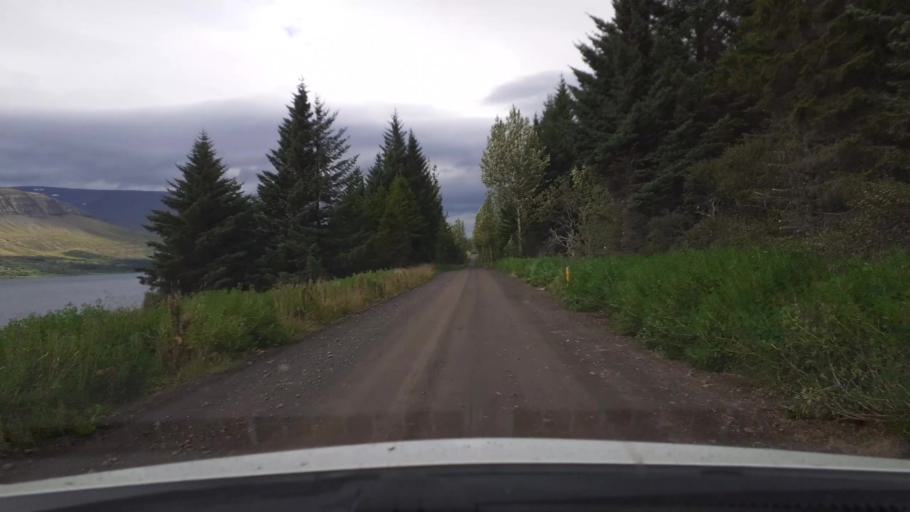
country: IS
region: Capital Region
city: Mosfellsbaer
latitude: 64.5210
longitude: -21.4512
